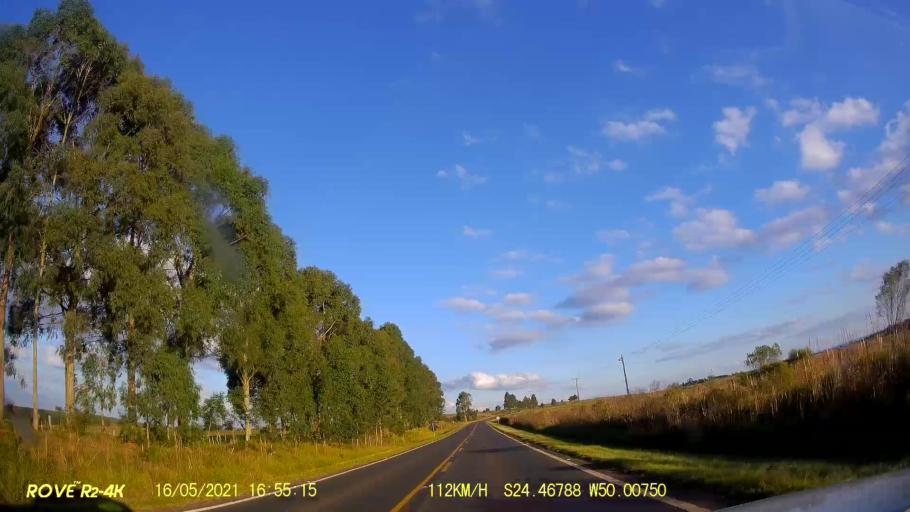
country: BR
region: Parana
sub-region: Pirai Do Sul
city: Pirai do Sul
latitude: -24.4678
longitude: -50.0075
